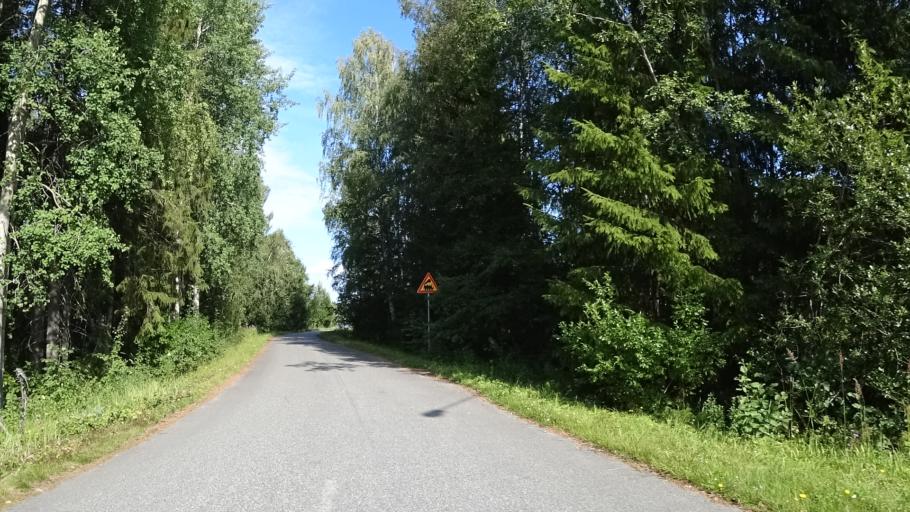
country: FI
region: North Karelia
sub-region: Joensuu
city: Eno
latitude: 62.8010
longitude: 30.1171
